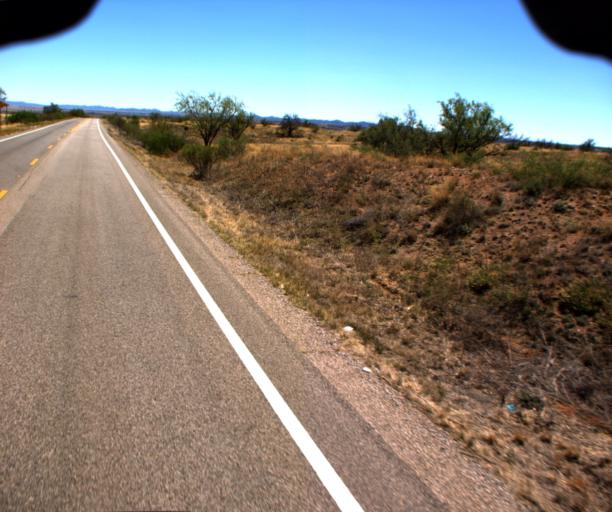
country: US
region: Arizona
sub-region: Pima County
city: Corona de Tucson
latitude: 31.7683
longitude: -110.6825
